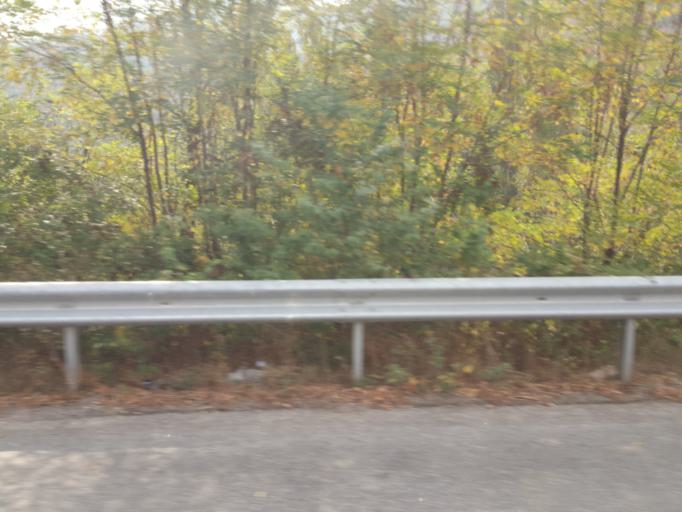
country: TR
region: Amasya
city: Gediksaray
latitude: 40.4891
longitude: 35.7859
